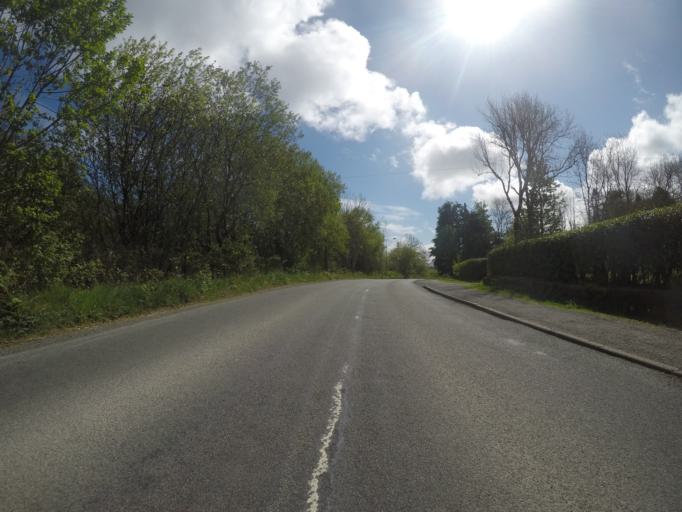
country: GB
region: Scotland
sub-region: Highland
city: Portree
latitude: 57.4177
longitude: -6.1916
